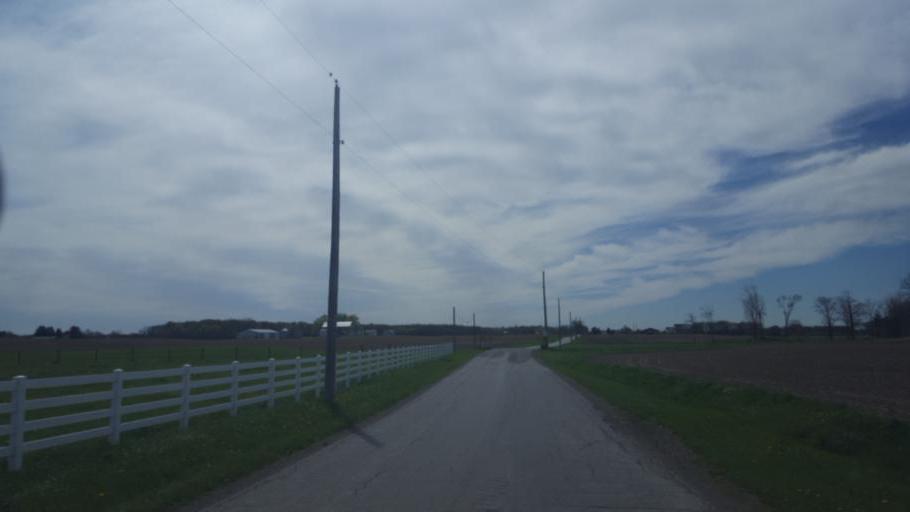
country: US
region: Ohio
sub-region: Richland County
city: Shelby
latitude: 40.8992
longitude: -82.6187
